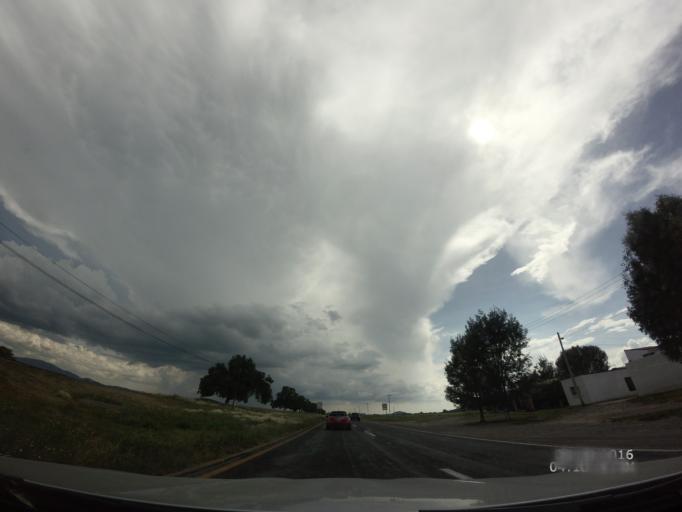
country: MX
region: Hidalgo
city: Zapotlan de Juarez
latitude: 19.9656
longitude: -98.8587
